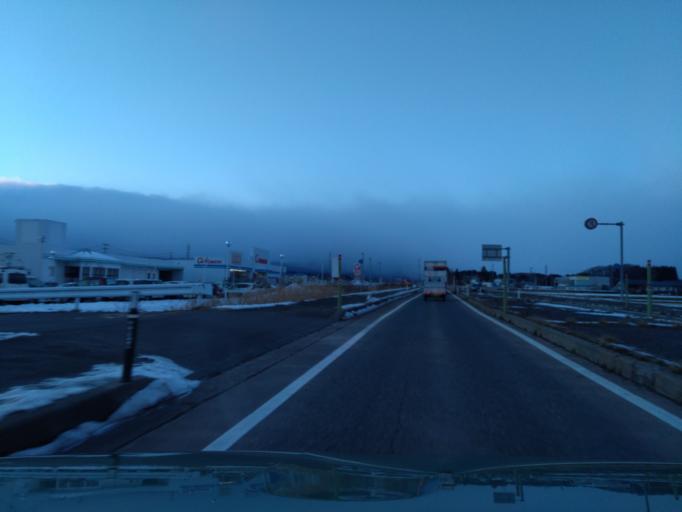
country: JP
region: Iwate
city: Shizukuishi
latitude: 39.6962
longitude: 140.9788
